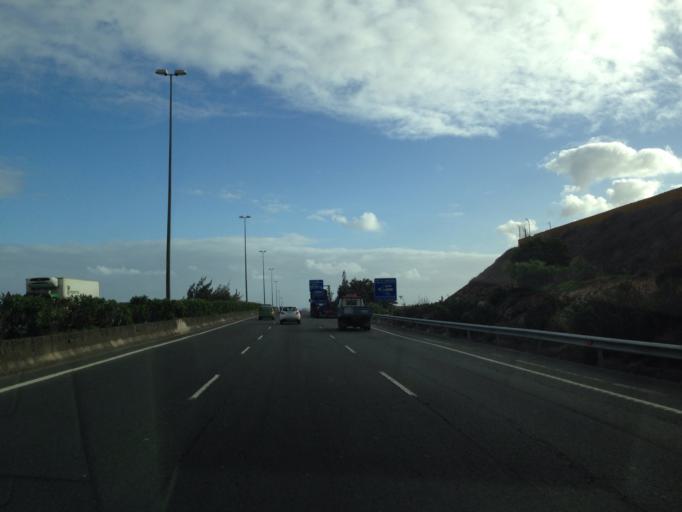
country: ES
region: Canary Islands
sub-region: Provincia de Las Palmas
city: Telde
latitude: 27.9606
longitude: -15.3891
